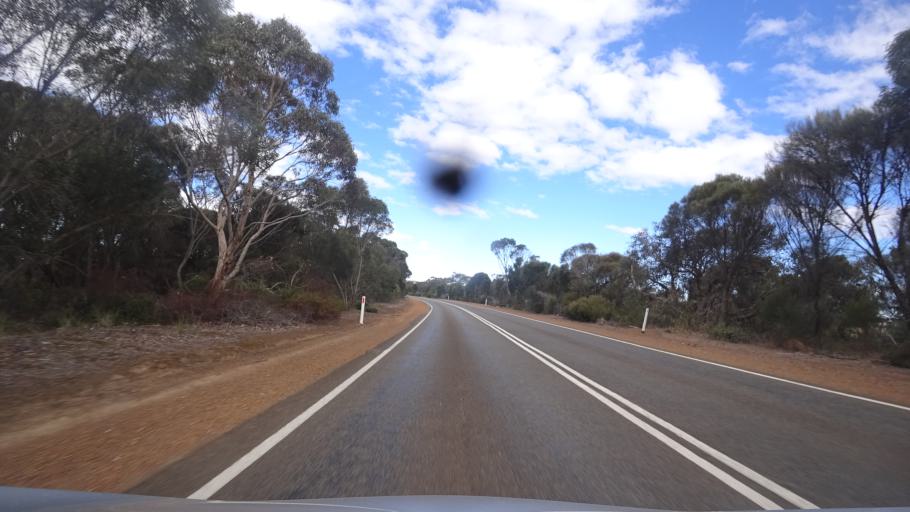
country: AU
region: South Australia
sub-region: Kangaroo Island
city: Kingscote
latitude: -35.7612
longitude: 137.3743
